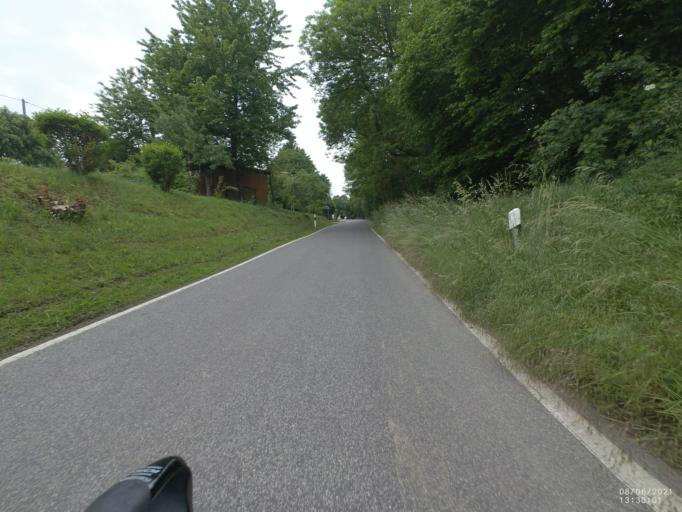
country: DE
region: Rheinland-Pfalz
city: Munstermaifeld
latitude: 50.2405
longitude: 7.3842
